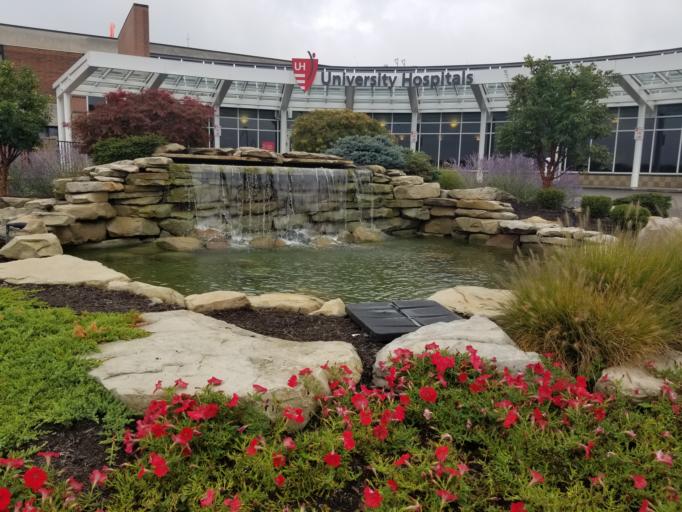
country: US
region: Ohio
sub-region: Geauga County
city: Burton
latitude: 41.5088
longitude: -81.1892
